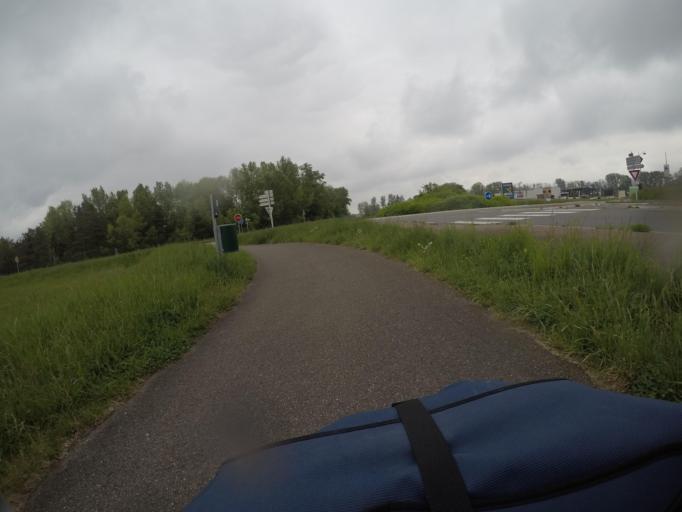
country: FR
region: Alsace
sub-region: Departement du Bas-Rhin
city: Roppenheim
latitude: 48.8186
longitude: 8.0194
